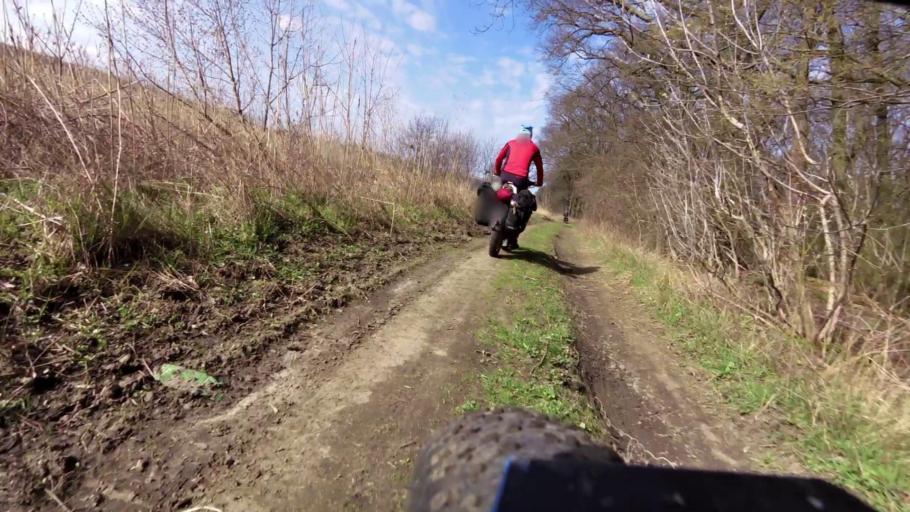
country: PL
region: Lubusz
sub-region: Powiat slubicki
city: Slubice
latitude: 52.3254
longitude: 14.5737
